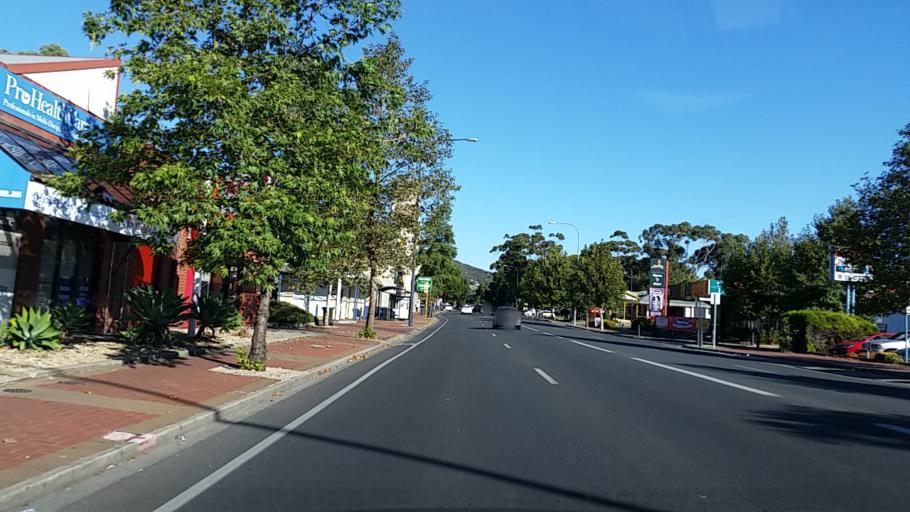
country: AU
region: South Australia
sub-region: Mitcham
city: Hawthorn
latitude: -34.9748
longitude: 138.6094
